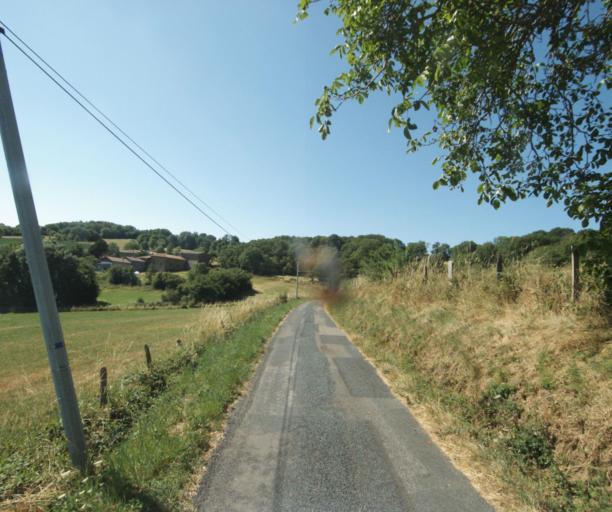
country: FR
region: Rhone-Alpes
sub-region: Departement du Rhone
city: Montrottier
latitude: 45.8122
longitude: 4.4904
